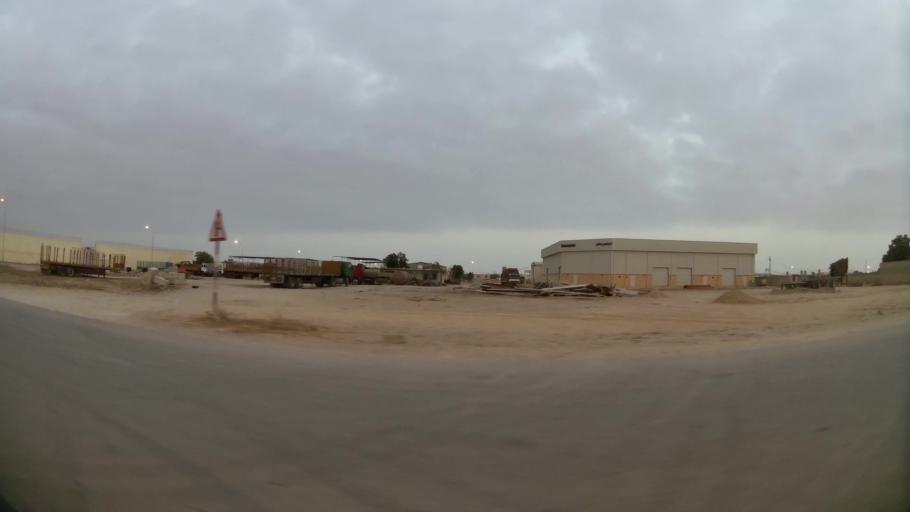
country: OM
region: Zufar
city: Salalah
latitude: 17.0348
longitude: 54.0406
